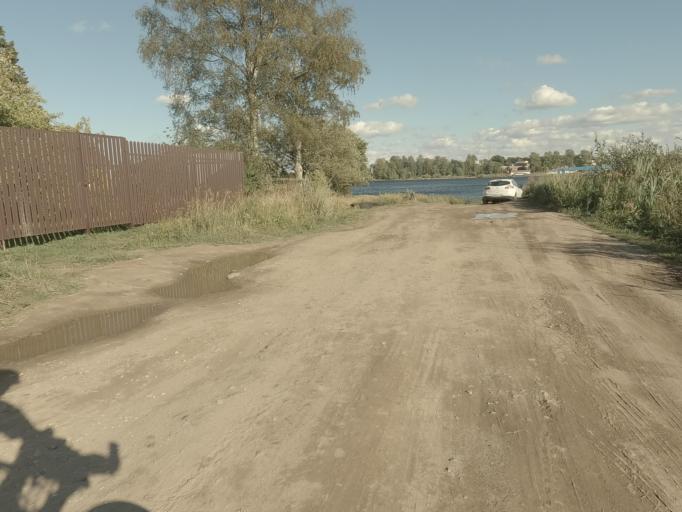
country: RU
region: Leningrad
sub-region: Volosovskiy Rayon
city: Shlissel'burg
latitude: 59.9517
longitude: 31.0241
